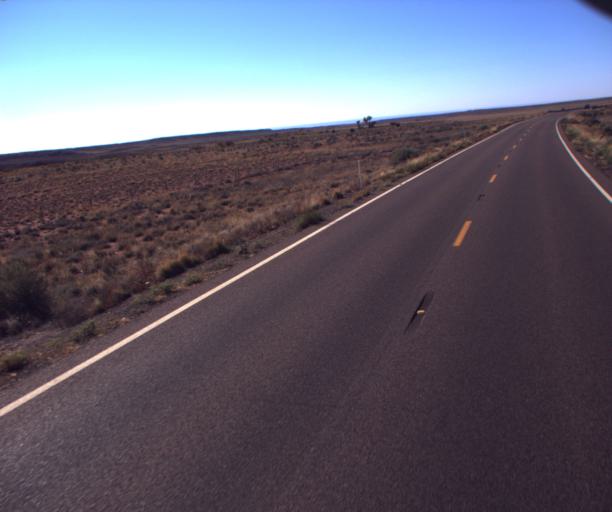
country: US
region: Arizona
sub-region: Navajo County
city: Joseph City
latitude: 35.1732
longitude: -110.4444
